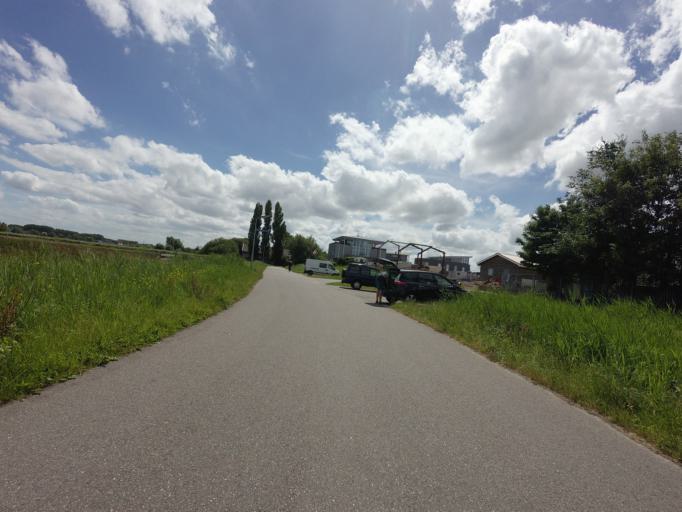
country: NL
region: North Holland
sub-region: Gemeente Zaanstad
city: Zaanstad
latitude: 52.4809
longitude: 4.8133
